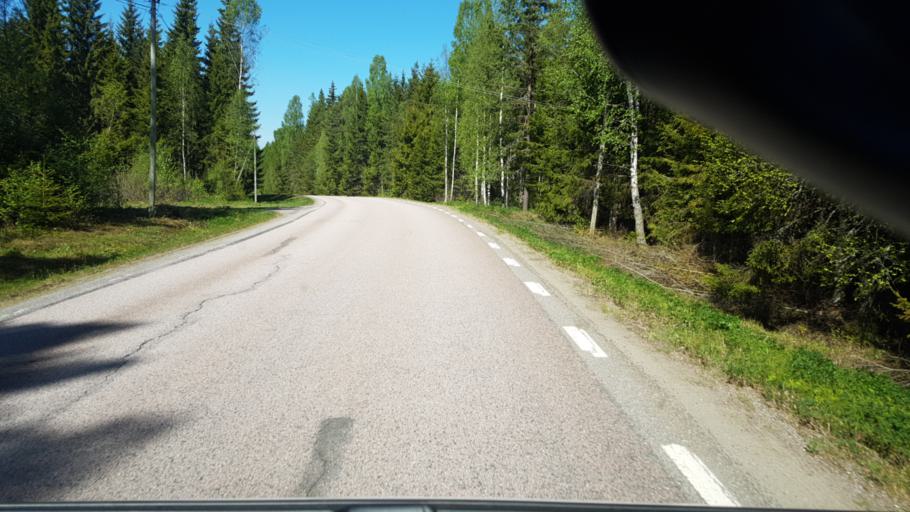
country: SE
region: Vaermland
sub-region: Eda Kommun
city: Amotfors
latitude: 59.8675
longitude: 12.4374
